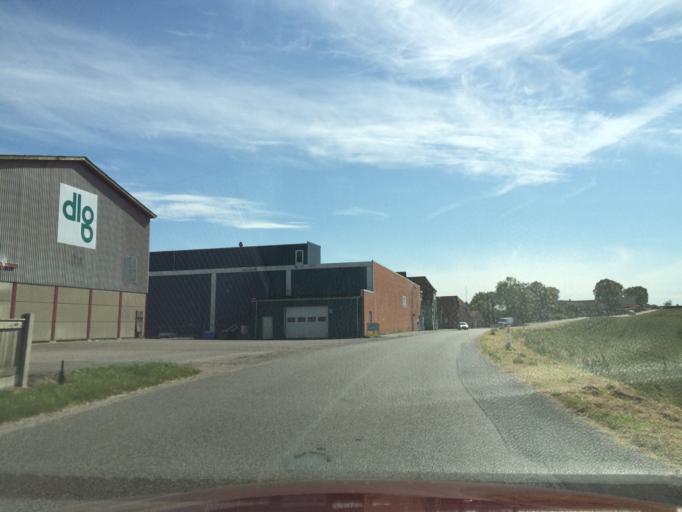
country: DK
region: Central Jutland
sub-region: Silkeborg Kommune
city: Silkeborg
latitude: 56.2205
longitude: 9.5611
